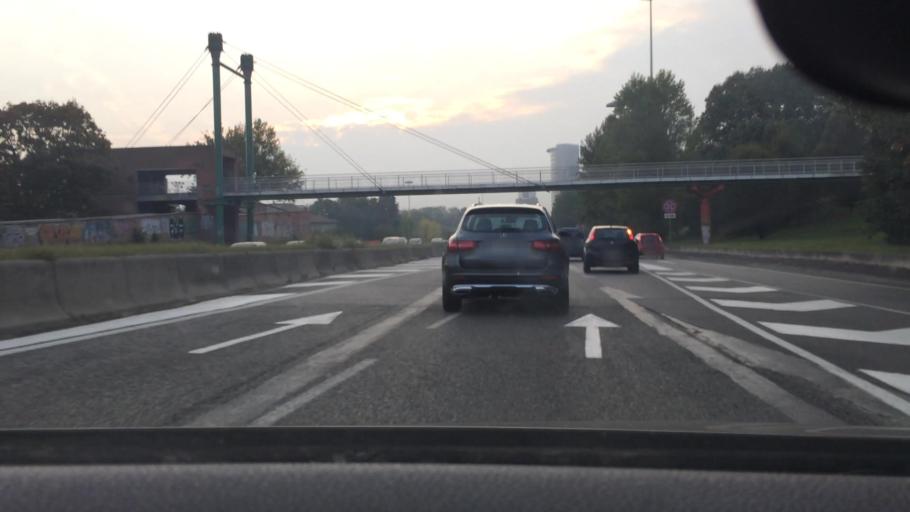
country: IT
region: Lombardy
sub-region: Citta metropolitana di Milano
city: Baranzate
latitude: 45.4938
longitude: 9.1331
